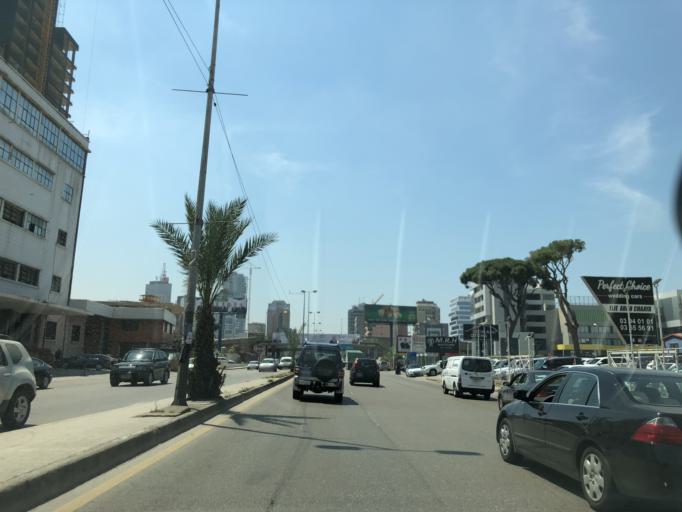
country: LB
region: Mont-Liban
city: Jdaidet el Matn
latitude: 33.8872
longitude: 35.5503
